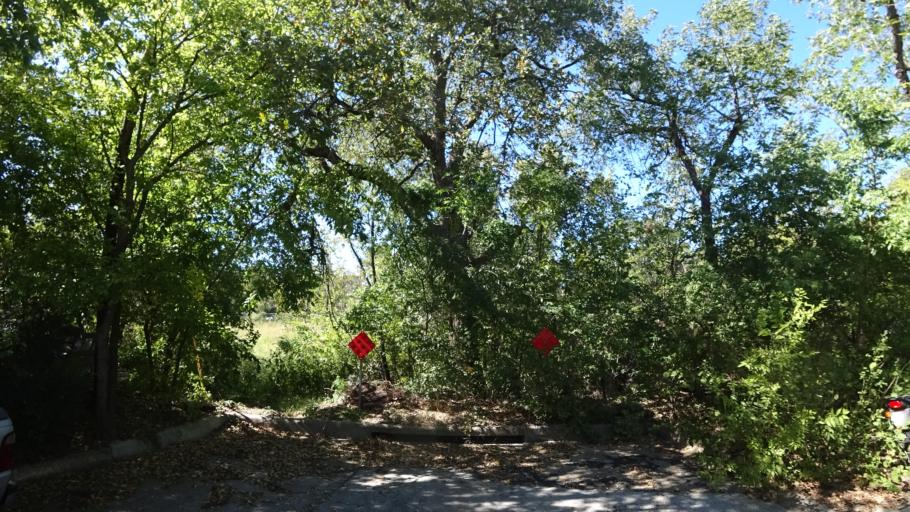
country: US
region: Texas
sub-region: Travis County
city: Austin
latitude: 30.2779
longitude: -97.7622
